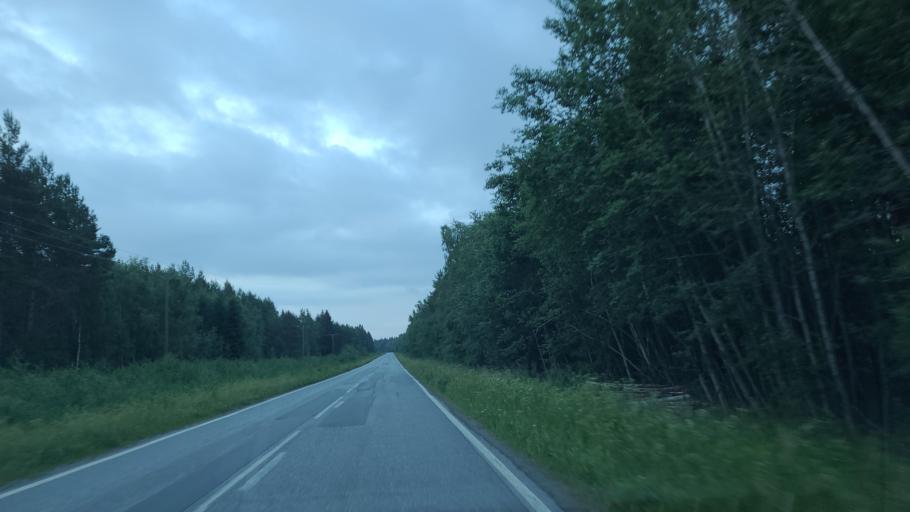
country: FI
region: Ostrobothnia
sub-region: Vaasa
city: Replot
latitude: 63.2182
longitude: 21.2477
